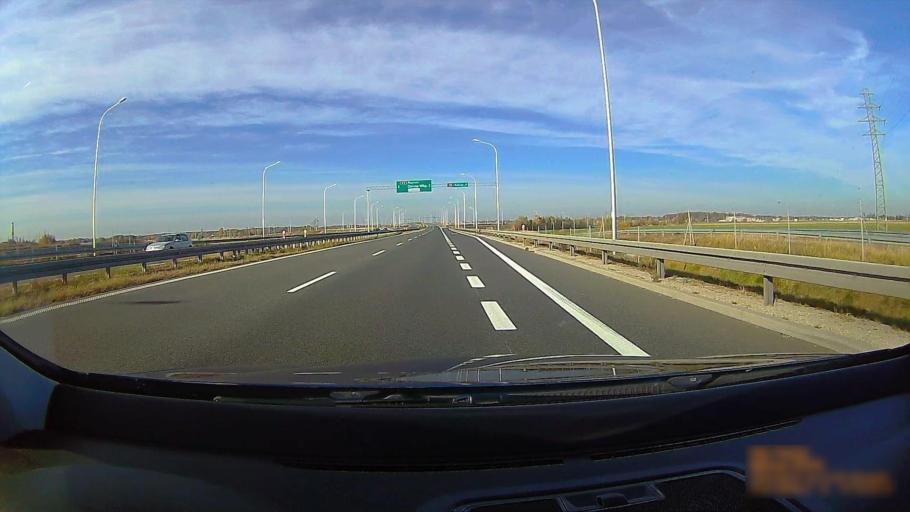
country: PL
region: Greater Poland Voivodeship
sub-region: Powiat ostrowski
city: Ostrow Wielkopolski
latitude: 51.6610
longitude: 17.8603
